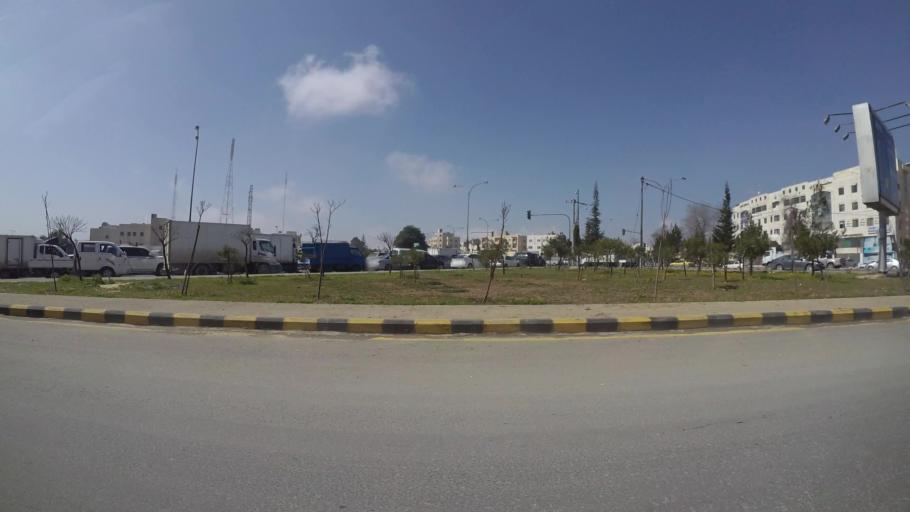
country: JO
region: Amman
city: Al Bunayyat ash Shamaliyah
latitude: 31.9066
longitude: 35.8863
